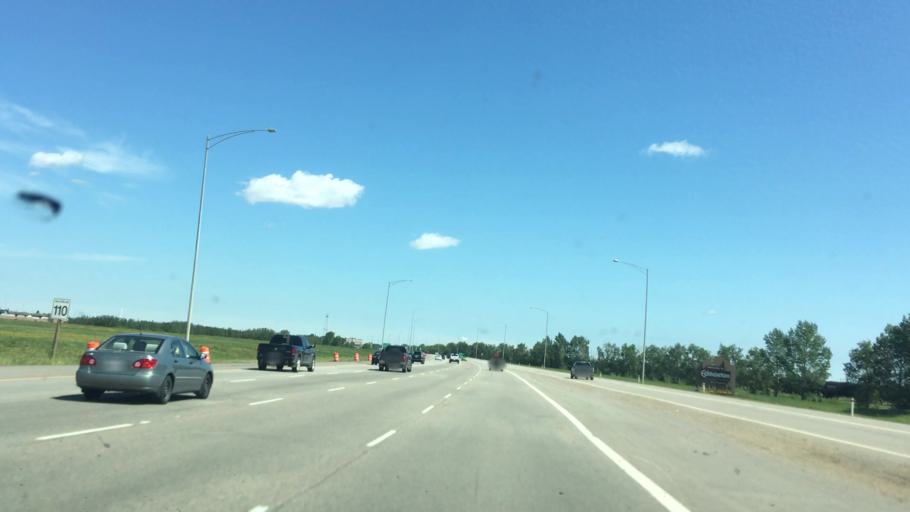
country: CA
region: Alberta
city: Beaumont
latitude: 53.4004
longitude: -113.5061
